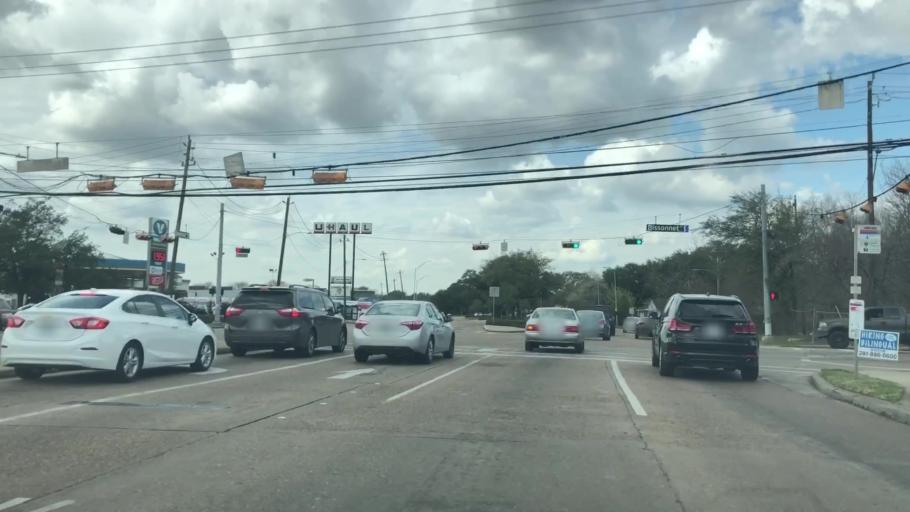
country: US
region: Texas
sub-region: Harris County
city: Bellaire
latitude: 29.6896
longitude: -95.5026
